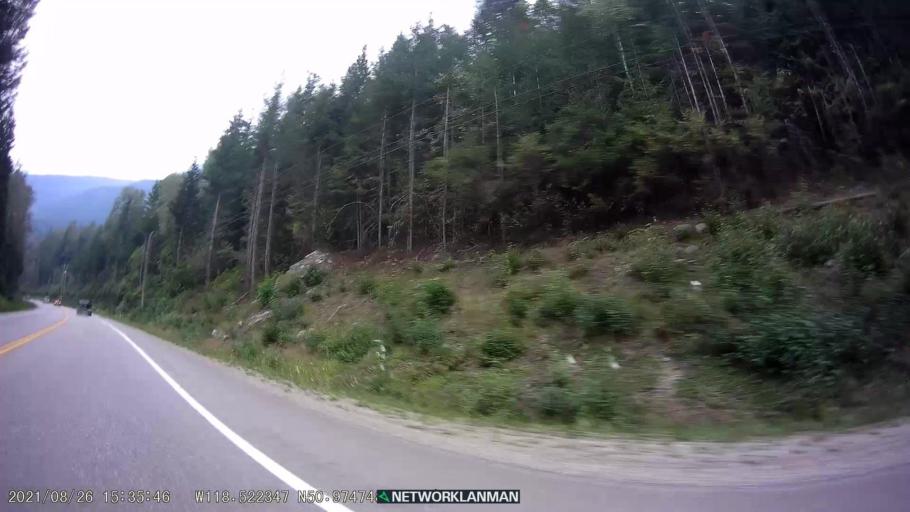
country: CA
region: British Columbia
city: Revelstoke
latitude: 50.9750
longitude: -118.5229
